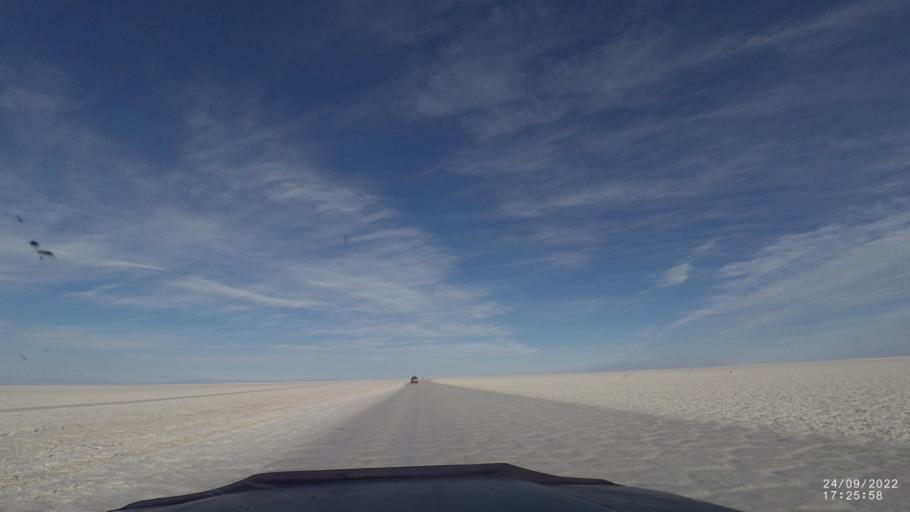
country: BO
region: Potosi
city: Colchani
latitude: -20.2918
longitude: -67.4772
